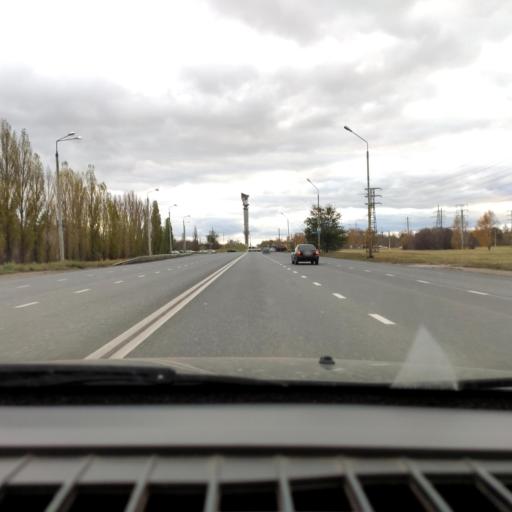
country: RU
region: Samara
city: Tol'yatti
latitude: 53.5559
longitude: 49.2883
